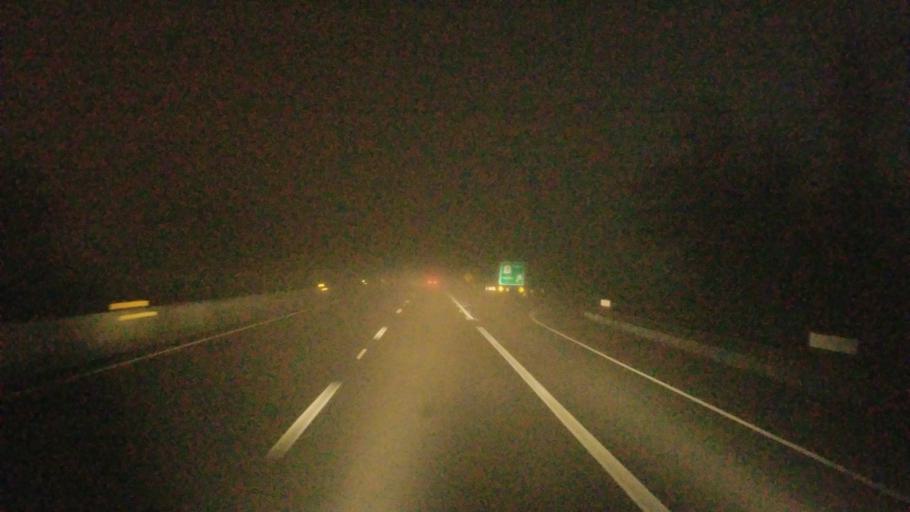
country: US
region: Pennsylvania
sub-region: Butler County
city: Butler
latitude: 40.8796
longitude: -79.9008
